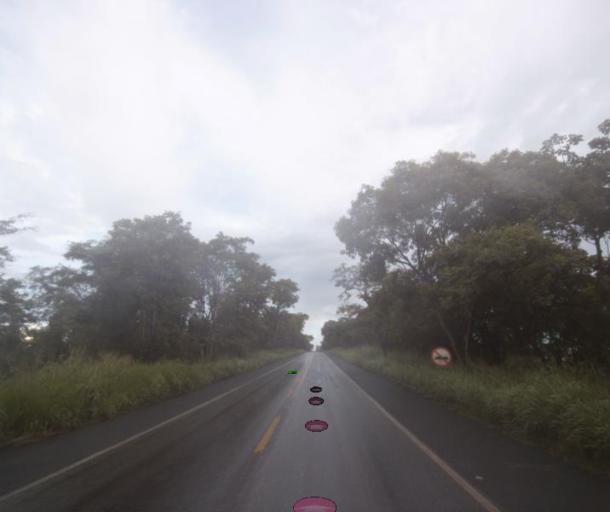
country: BR
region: Goias
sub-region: Porangatu
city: Porangatu
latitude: -13.8062
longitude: -49.0381
